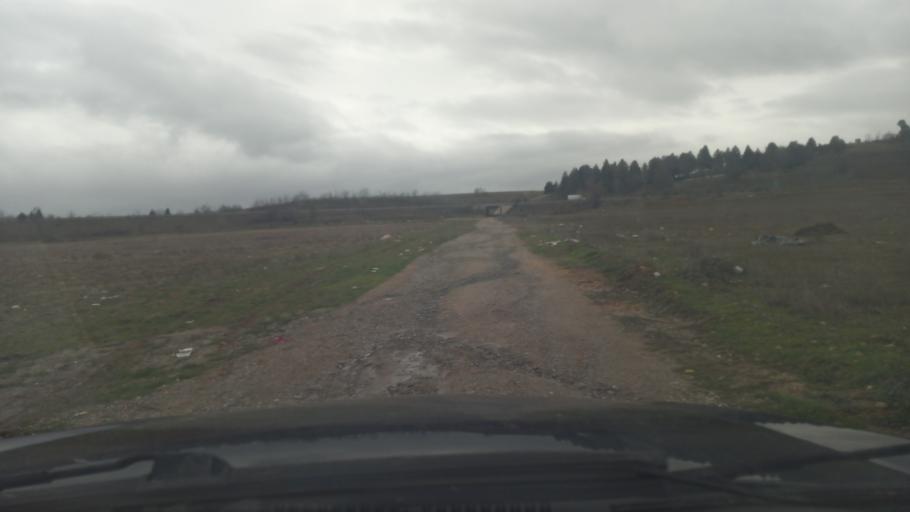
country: MK
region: Gradsko
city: Gradsko
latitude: 41.5779
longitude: 21.9341
